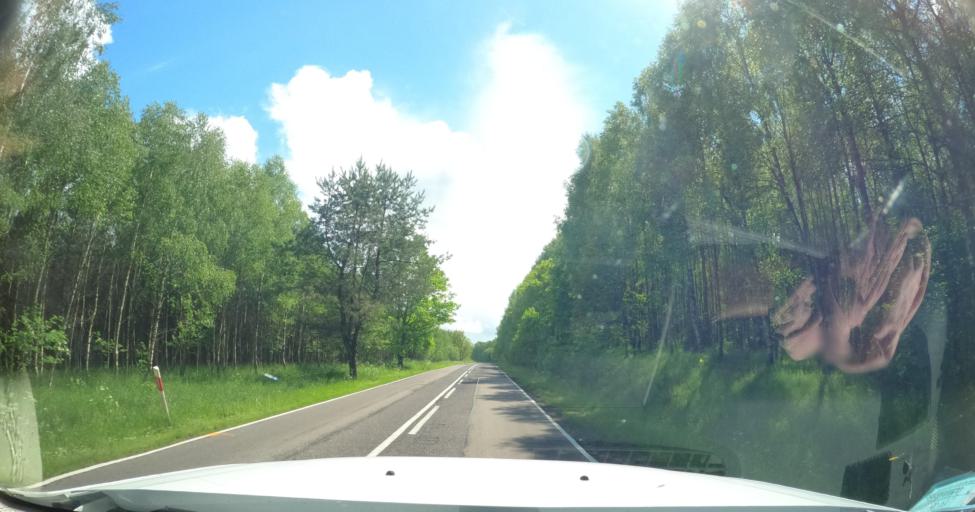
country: PL
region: Pomeranian Voivodeship
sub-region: Powiat bytowski
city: Czarna Dabrowka
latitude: 54.3729
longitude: 17.5006
